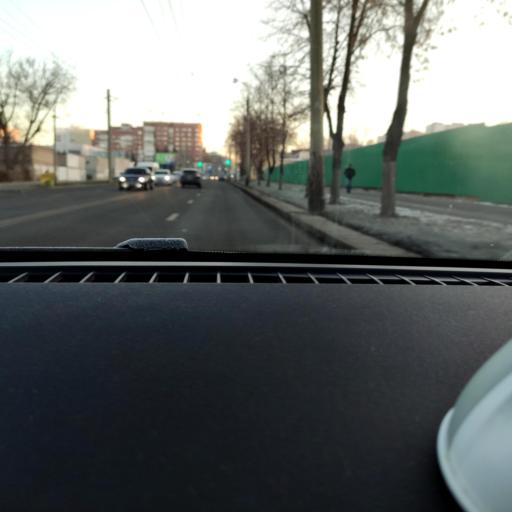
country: RU
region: Samara
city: Samara
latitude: 53.2089
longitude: 50.1498
